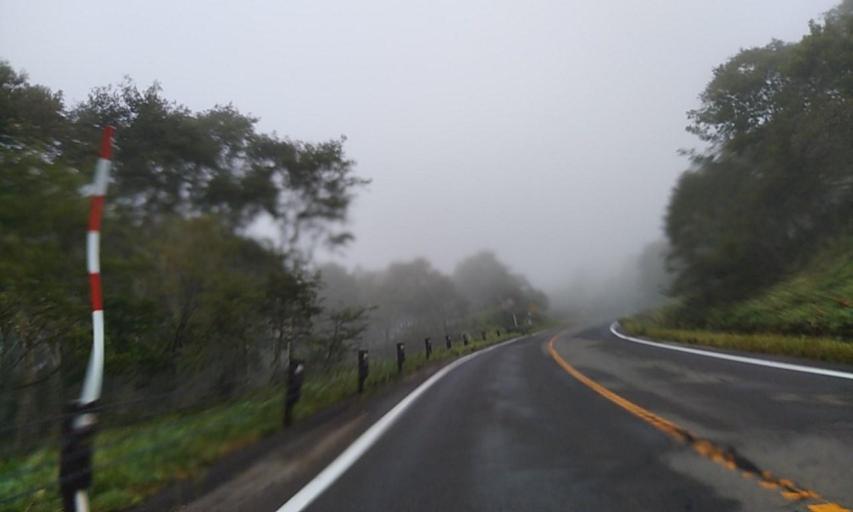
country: JP
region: Hokkaido
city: Bihoro
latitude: 43.5463
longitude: 144.5056
